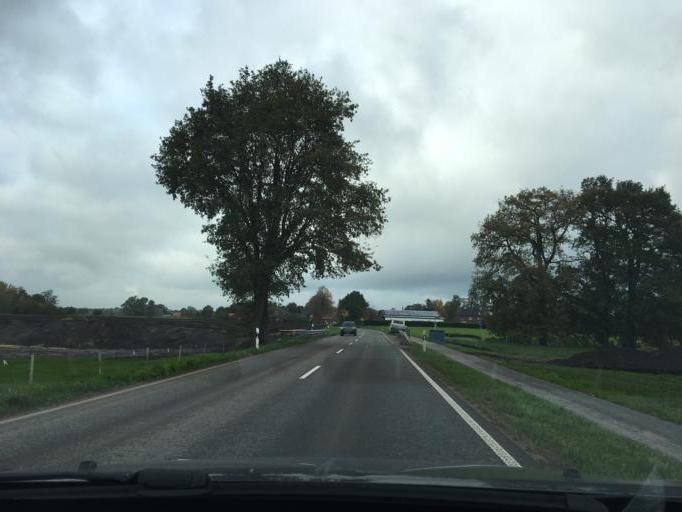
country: NL
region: Overijssel
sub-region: Gemeente Haaksbergen
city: Haaksbergen
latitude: 52.0948
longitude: 6.7629
